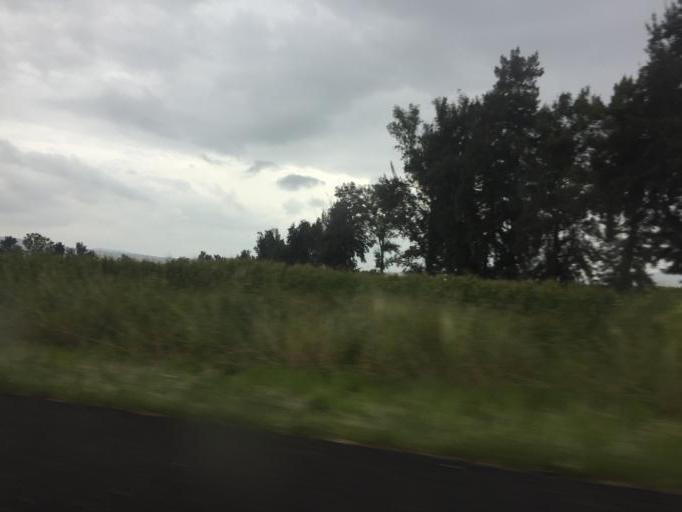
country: MX
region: Jalisco
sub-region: Zapotlan del Rey
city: Zapotlan del Rey
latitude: 20.4561
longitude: -102.8930
